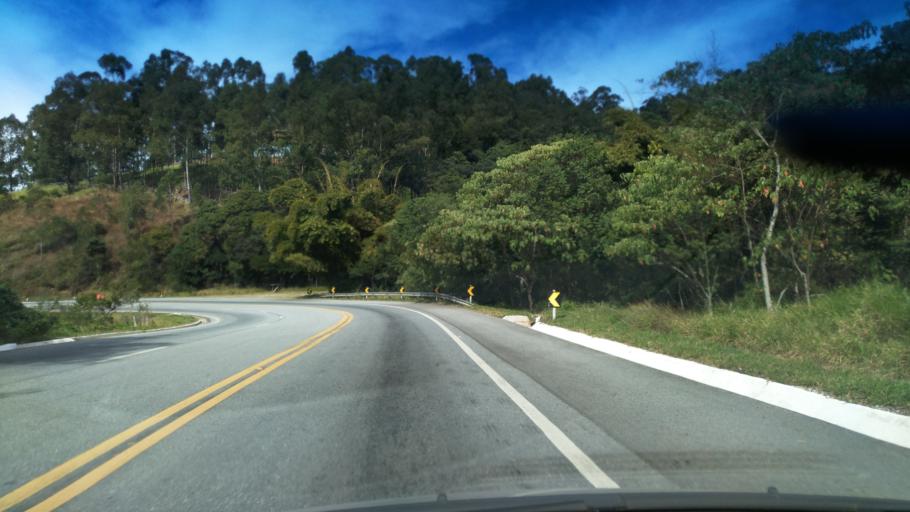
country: BR
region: Minas Gerais
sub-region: Borda Da Mata
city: Borda da Mata
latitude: -22.1340
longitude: -46.1496
